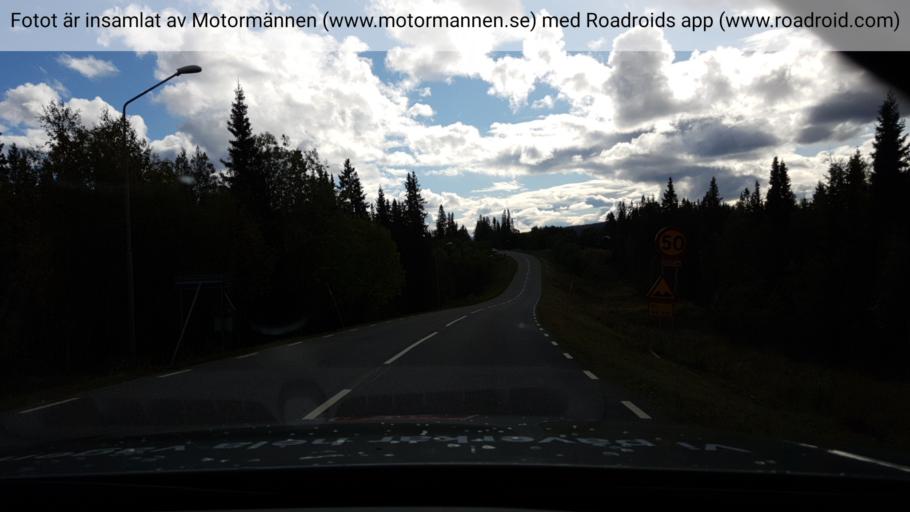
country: SE
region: Jaemtland
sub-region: Are Kommun
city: Are
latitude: 63.5637
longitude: 13.0257
